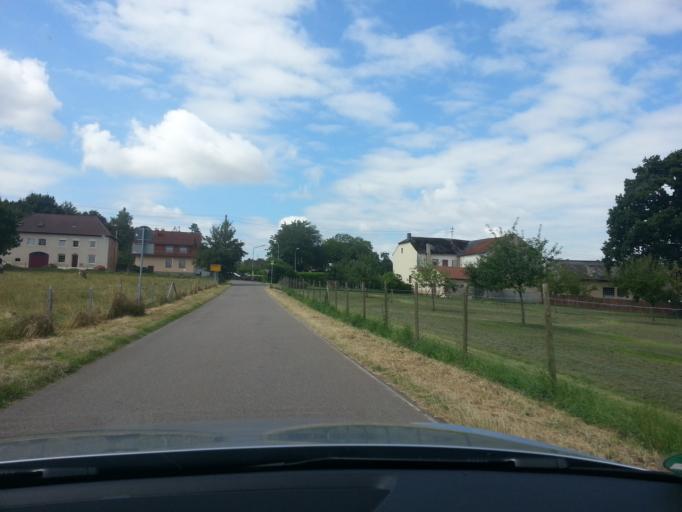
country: DE
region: Rheinland-Pfalz
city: Kirf
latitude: 49.5081
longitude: 6.4722
